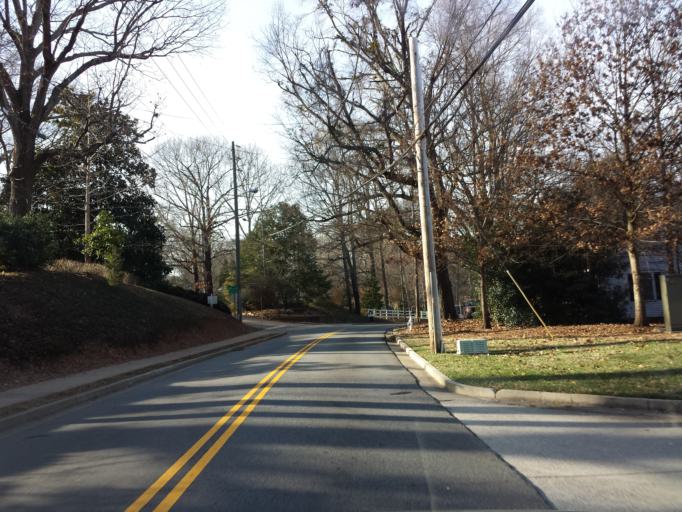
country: US
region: Georgia
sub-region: Cobb County
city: Marietta
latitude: 33.9645
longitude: -84.5594
